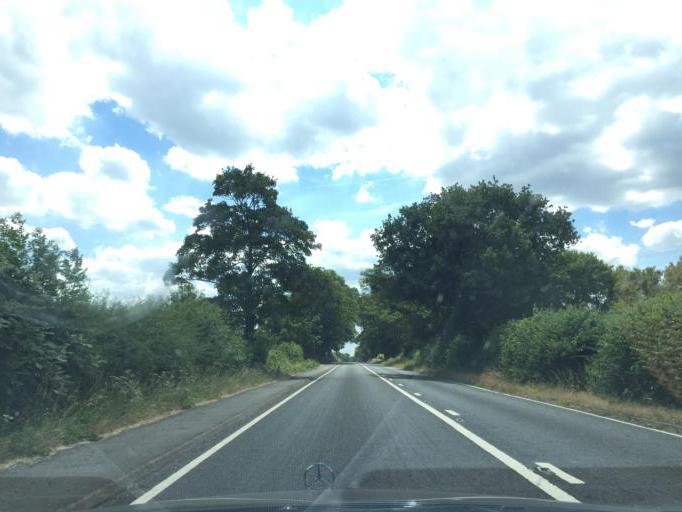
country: GB
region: England
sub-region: Leicestershire
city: Hinckley
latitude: 52.4796
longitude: -1.3728
